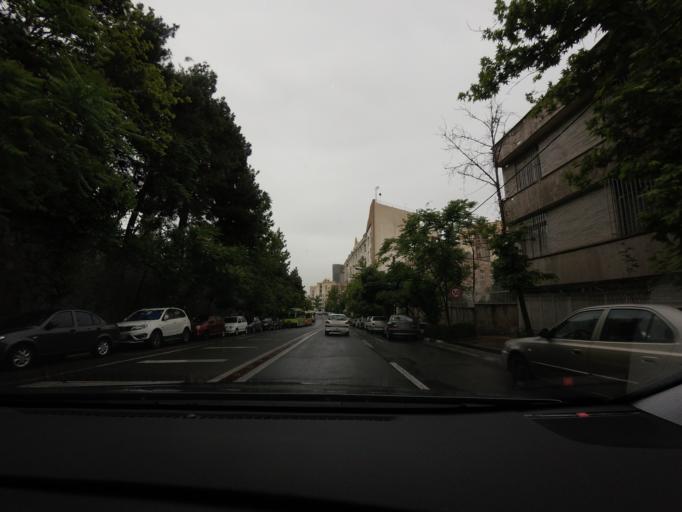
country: IR
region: Tehran
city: Tajrish
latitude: 35.7676
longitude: 51.4007
